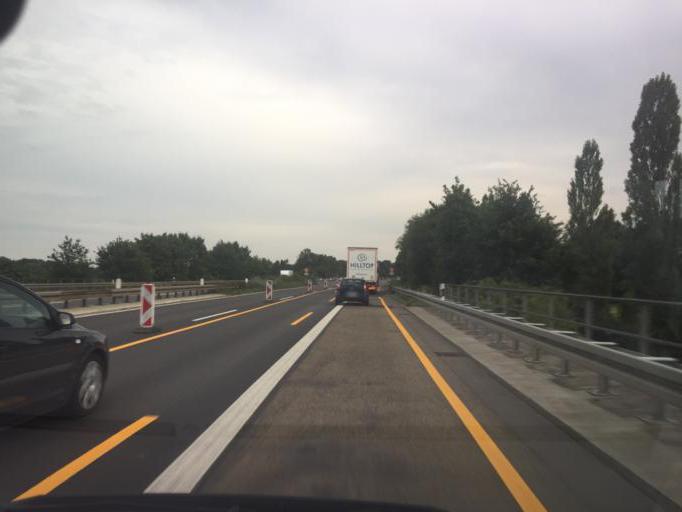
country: DE
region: North Rhine-Westphalia
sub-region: Regierungsbezirk Dusseldorf
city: Viersen
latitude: 51.2608
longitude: 6.3612
